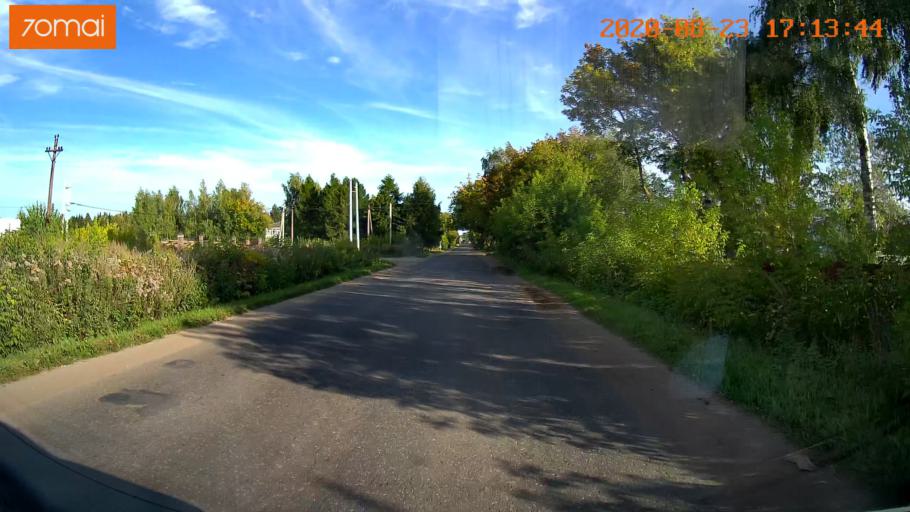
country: RU
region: Ivanovo
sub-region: Gorod Ivanovo
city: Ivanovo
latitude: 57.0517
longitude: 40.9226
